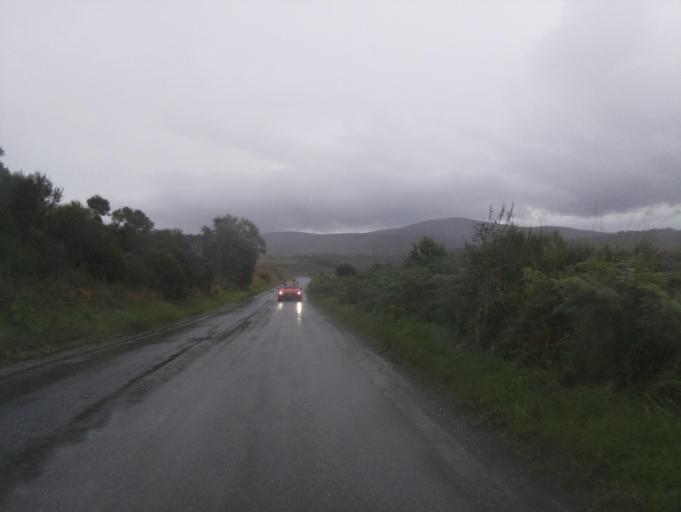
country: GB
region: Scotland
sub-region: Highland
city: Grantown on Spey
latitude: 57.3054
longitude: -3.5737
